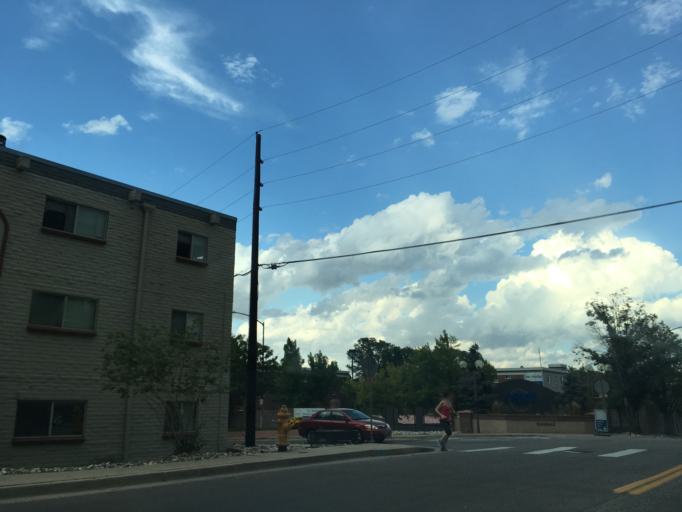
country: US
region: Colorado
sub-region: Arapahoe County
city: Glendale
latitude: 39.6965
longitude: -104.9320
